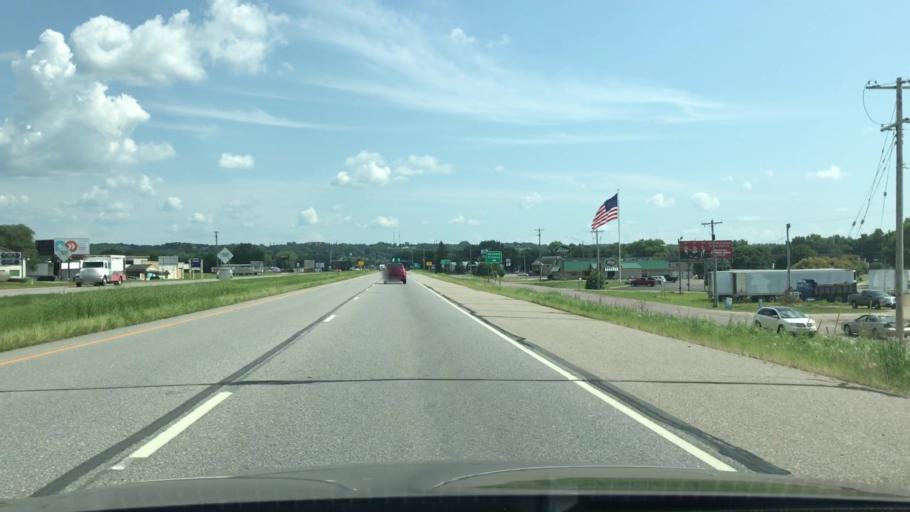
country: US
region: Minnesota
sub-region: Blue Earth County
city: Mankato
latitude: 44.1851
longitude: -94.0113
